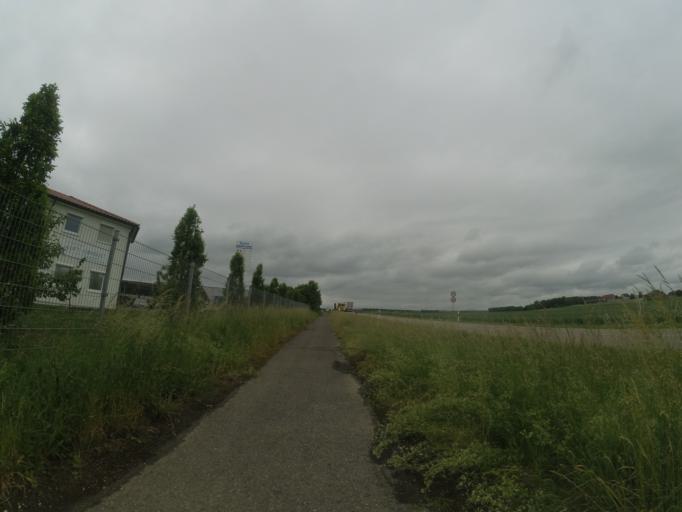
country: DE
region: Baden-Wuerttemberg
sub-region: Tuebingen Region
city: Nerenstetten
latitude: 48.4981
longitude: 10.0800
